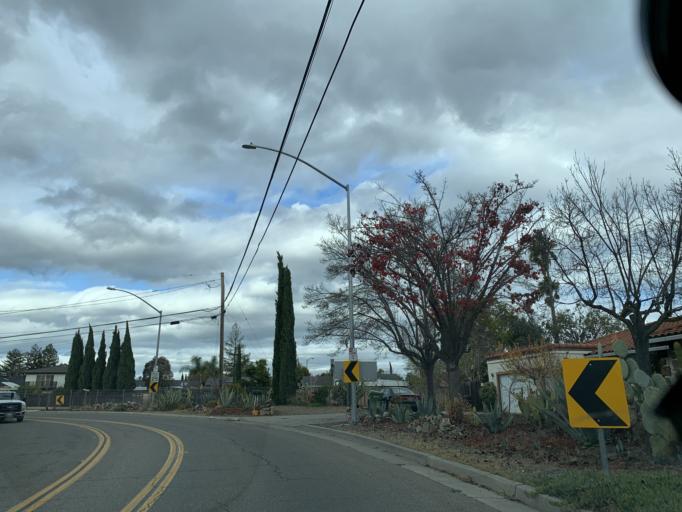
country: US
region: California
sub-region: Santa Clara County
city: Campbell
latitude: 37.2769
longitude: -121.9710
